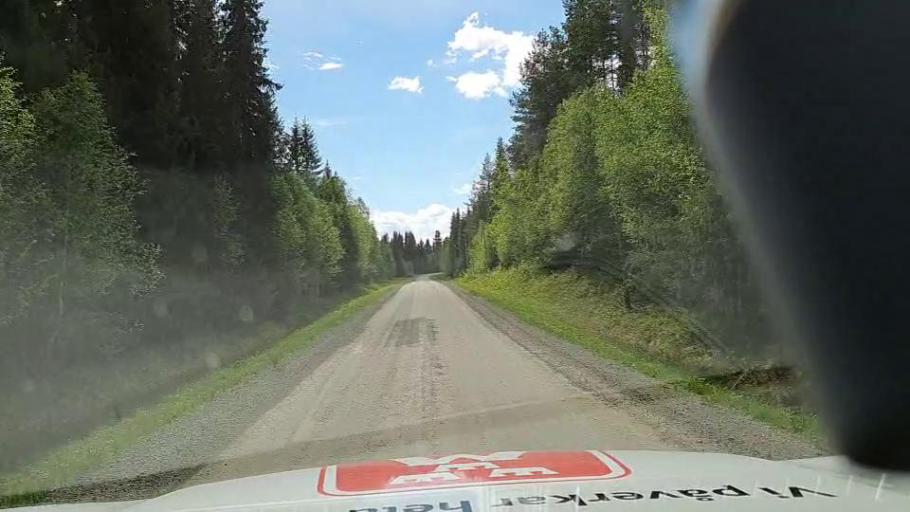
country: SE
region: Vaesterbotten
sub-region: Vilhelmina Kommun
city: Sjoberg
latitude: 64.5482
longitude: 15.7937
